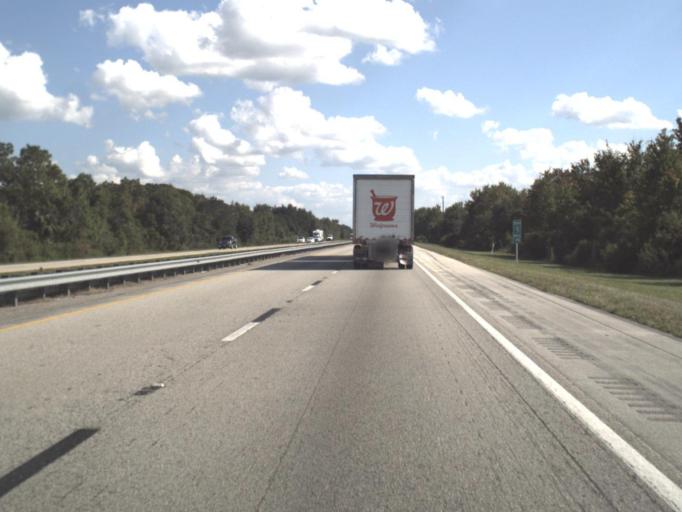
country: US
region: Florida
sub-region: Indian River County
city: Fellsmere
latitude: 27.7496
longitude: -80.9373
